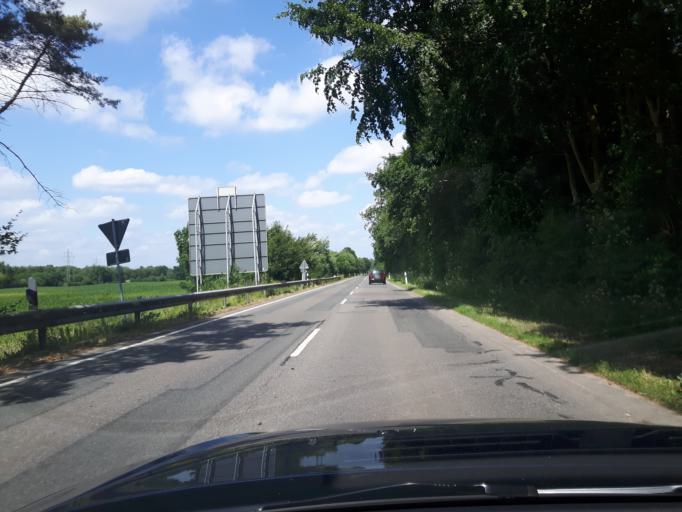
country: DE
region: Schleswig-Holstein
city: Scharbeutz
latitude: 54.0545
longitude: 10.7417
